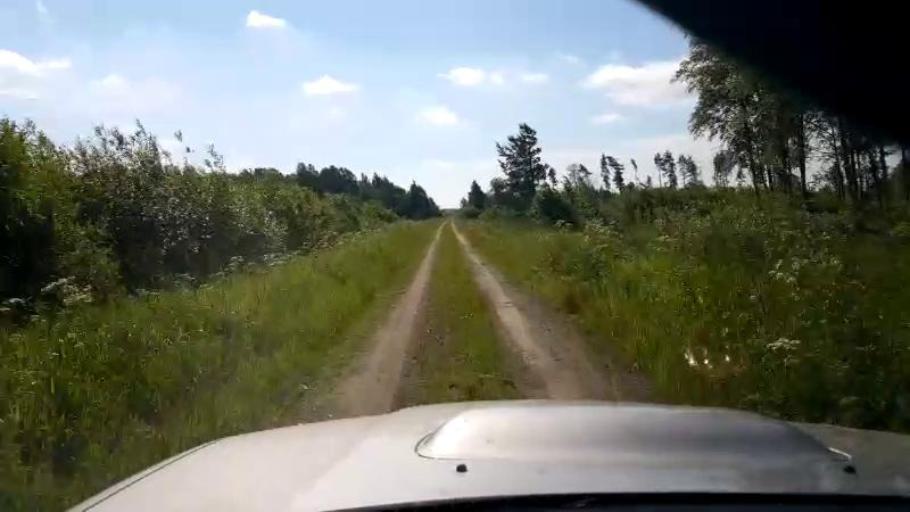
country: EE
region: Paernumaa
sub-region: Sindi linn
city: Sindi
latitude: 58.5026
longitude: 24.6437
